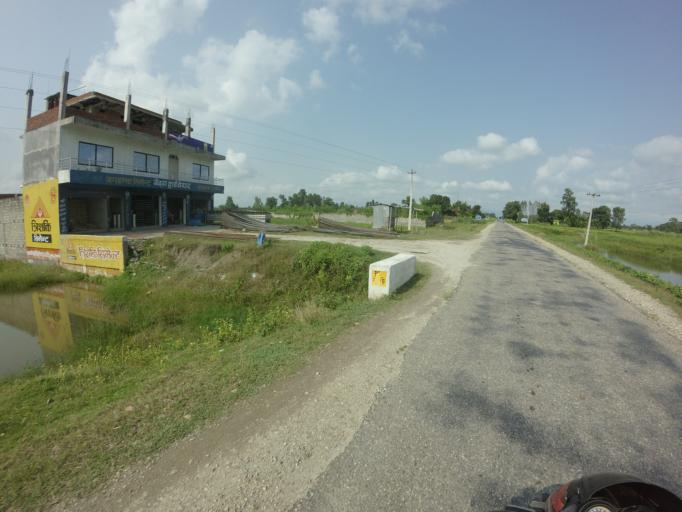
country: NP
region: Far Western
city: Tikapur
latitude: 28.4760
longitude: 81.0745
